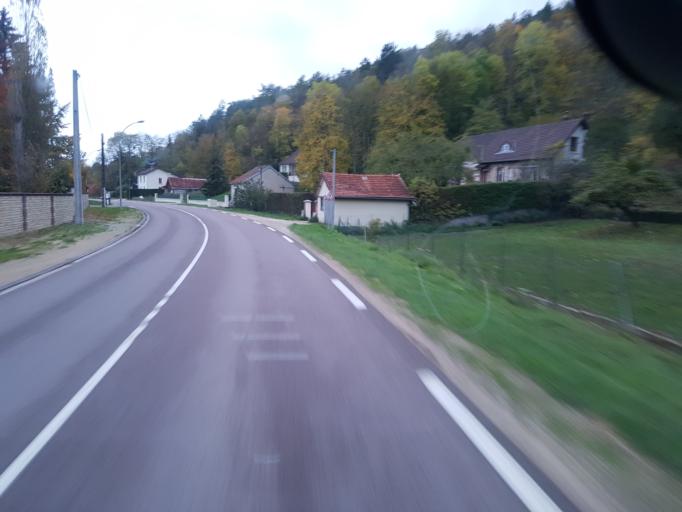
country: FR
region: Champagne-Ardenne
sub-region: Departement de l'Aube
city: Mussy-sur-Seine
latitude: 47.9835
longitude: 4.4959
